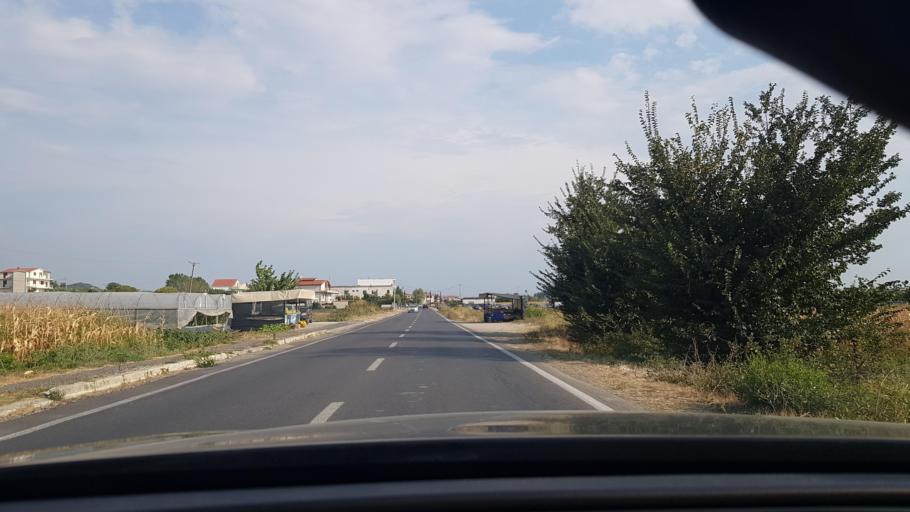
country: AL
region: Durres
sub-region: Rrethi i Durresit
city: Manze
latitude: 41.4528
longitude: 19.5690
